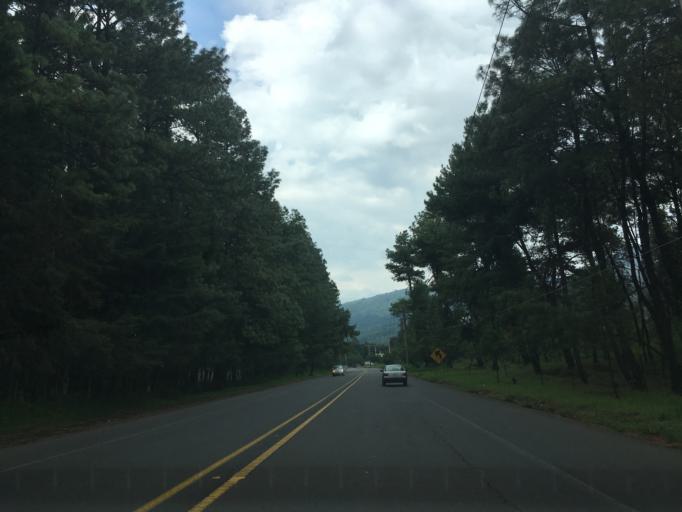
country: MX
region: Michoacan
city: Capacuaro
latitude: 19.5305
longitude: -102.0794
